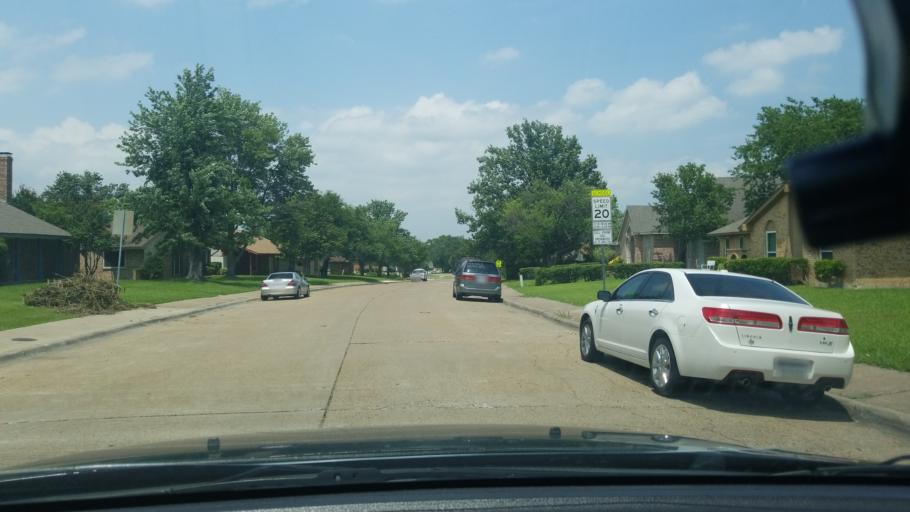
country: US
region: Texas
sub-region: Dallas County
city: Mesquite
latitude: 32.8070
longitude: -96.6445
